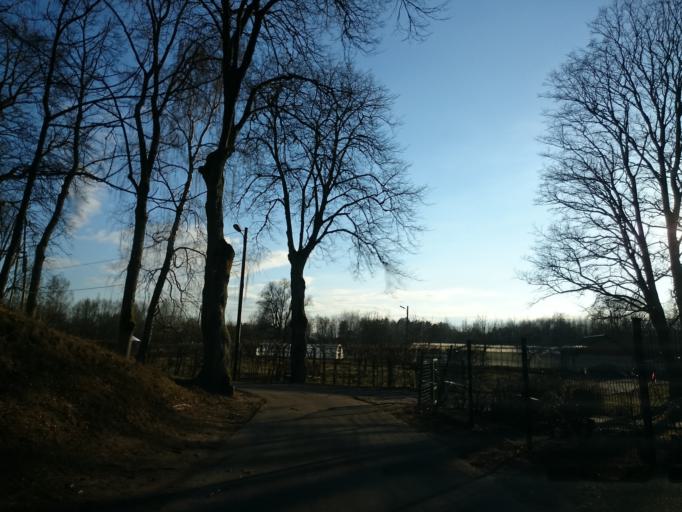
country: LV
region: Carnikava
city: Carnikava
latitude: 57.1255
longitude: 24.3207
